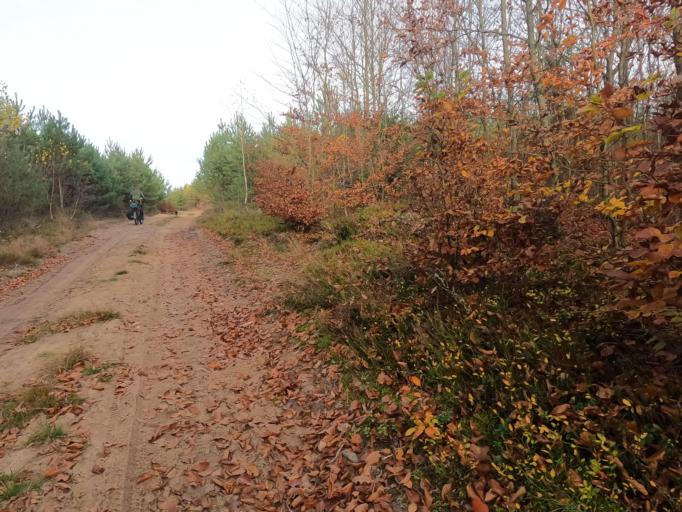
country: PL
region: Pomeranian Voivodeship
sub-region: Powiat starogardzki
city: Skarszewy
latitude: 54.0125
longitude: 18.4632
